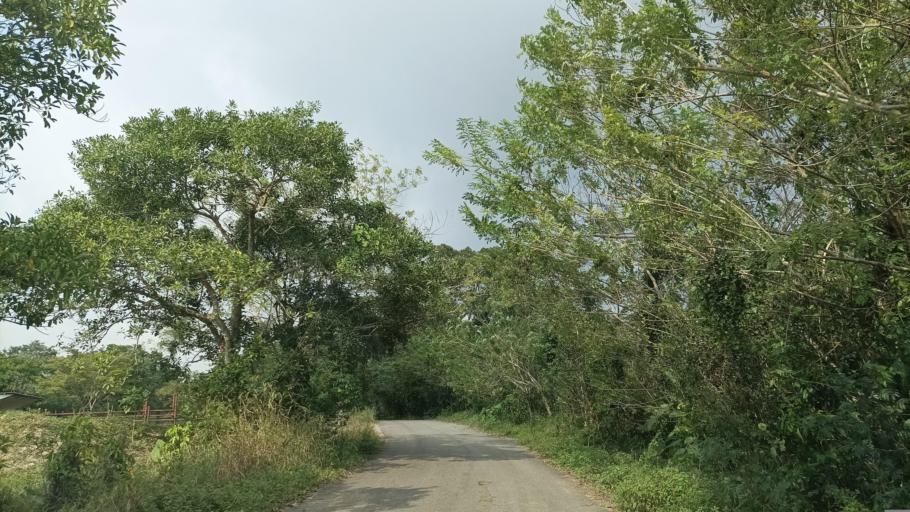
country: MX
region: Veracruz
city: Allende
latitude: 18.1056
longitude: -94.2936
